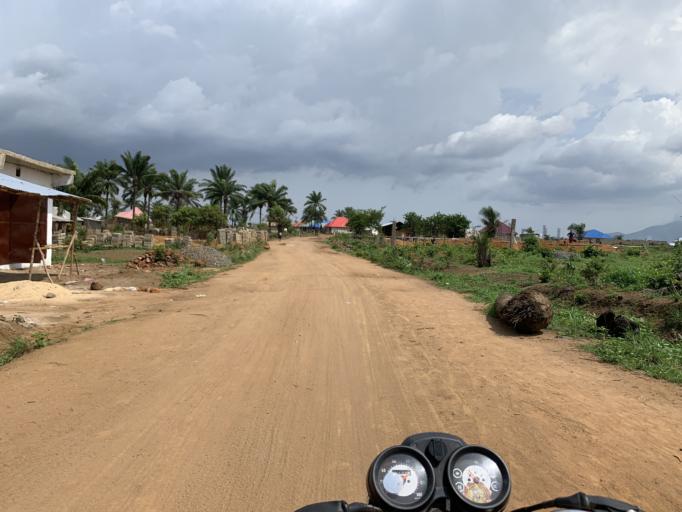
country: SL
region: Western Area
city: Waterloo
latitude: 8.3576
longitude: -13.0446
